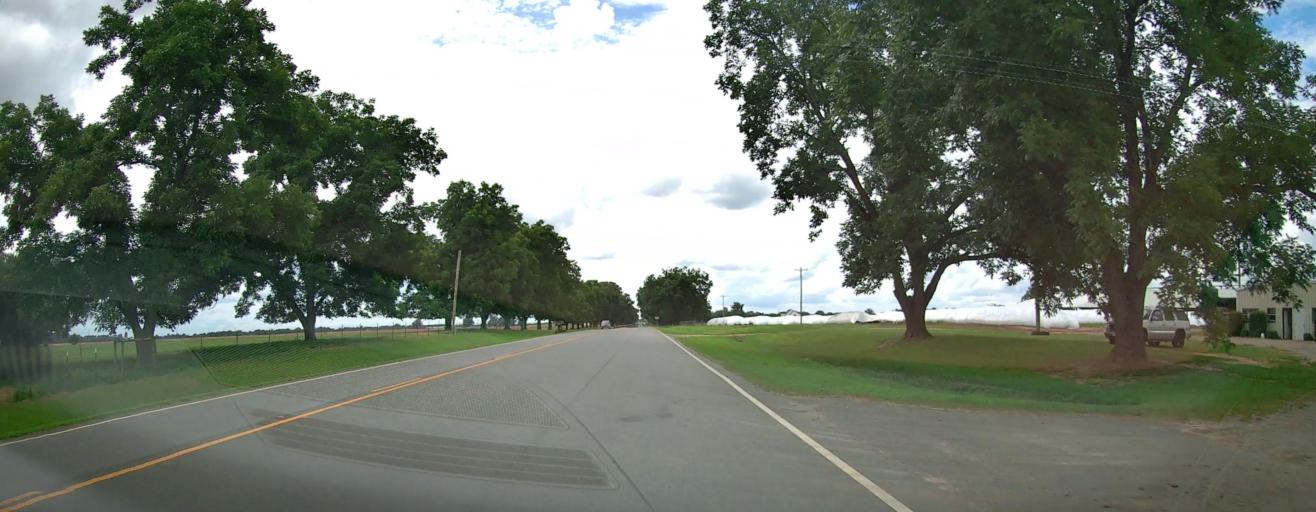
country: US
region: Georgia
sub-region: Macon County
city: Montezuma
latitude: 32.2931
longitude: -83.9584
